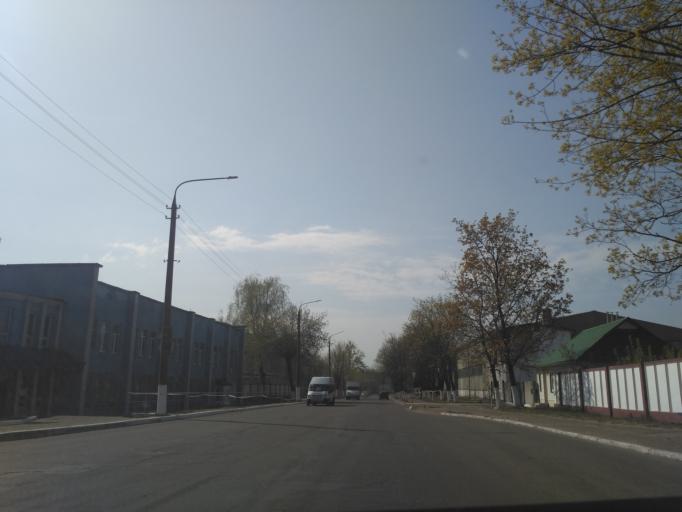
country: BY
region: Minsk
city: Horad Barysaw
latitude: 54.2027
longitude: 28.5162
